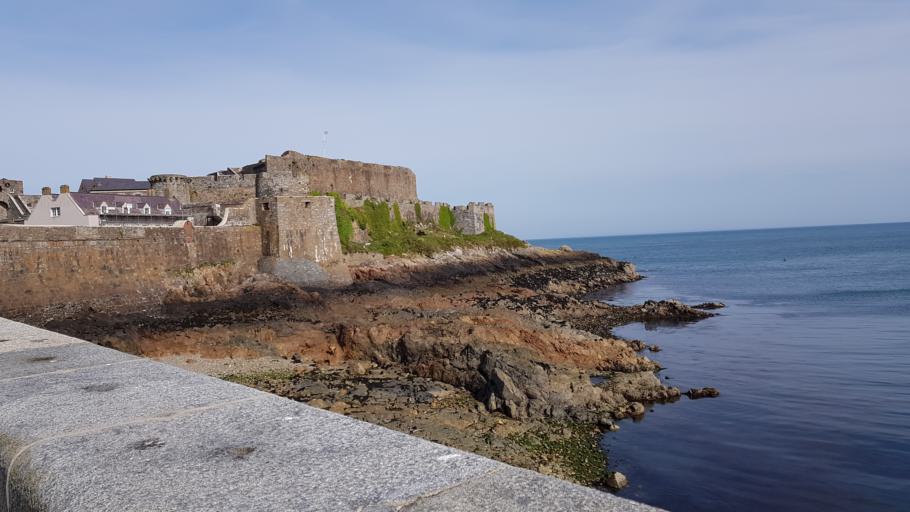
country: GG
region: St Peter Port
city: Saint Peter Port
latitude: 49.4533
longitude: -2.5288
